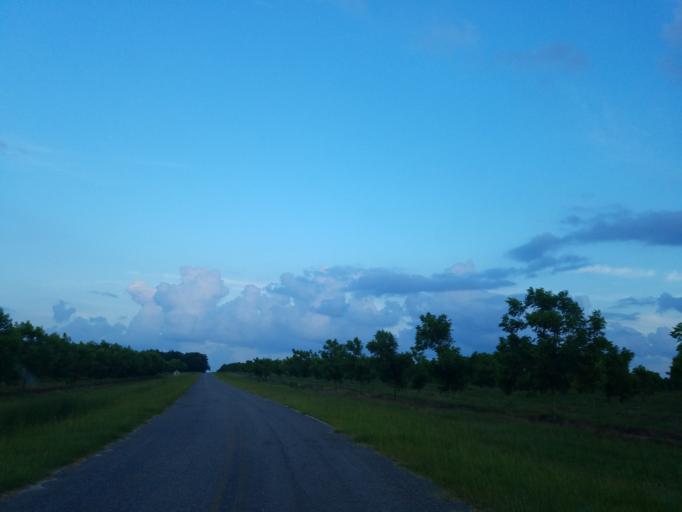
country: US
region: Georgia
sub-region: Dooly County
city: Unadilla
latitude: 32.1760
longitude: -83.7492
